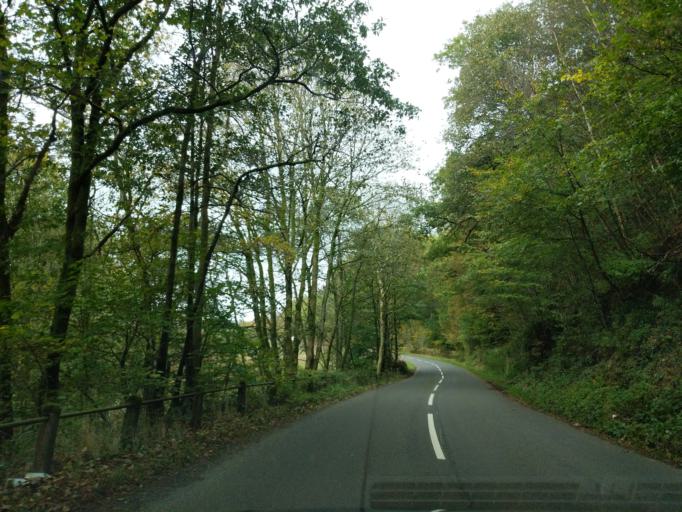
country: GB
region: Scotland
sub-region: Dumfries and Galloway
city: Thornhill
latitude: 55.2649
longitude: -3.7792
